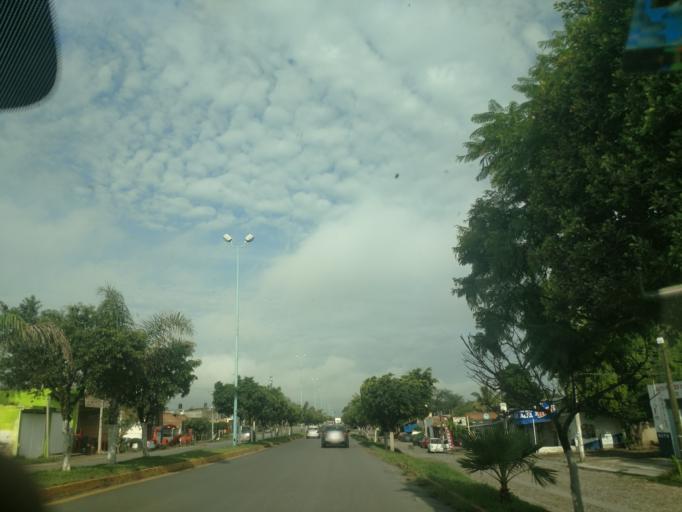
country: MX
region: Jalisco
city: Ameca
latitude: 20.5365
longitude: -104.0337
